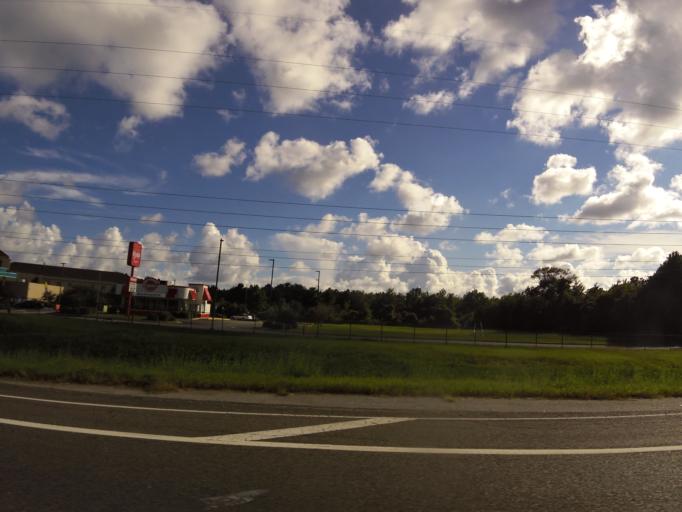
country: US
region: Georgia
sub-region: Glynn County
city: Brunswick
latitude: 31.1367
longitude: -81.5726
